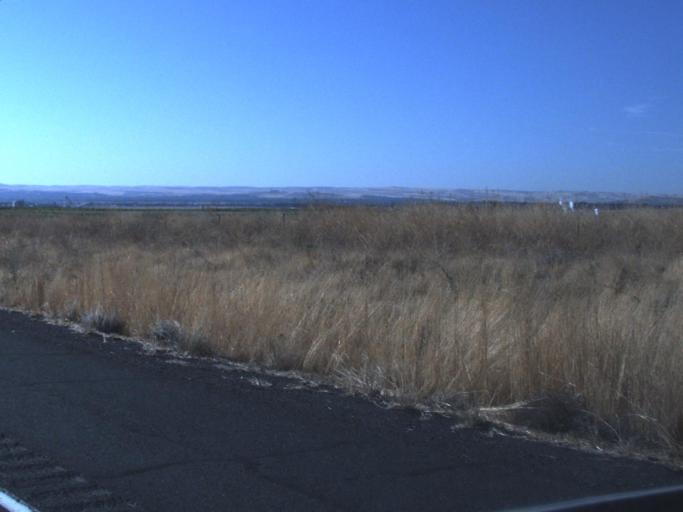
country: US
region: Washington
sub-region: Franklin County
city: Pasco
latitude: 46.2976
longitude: -119.0937
